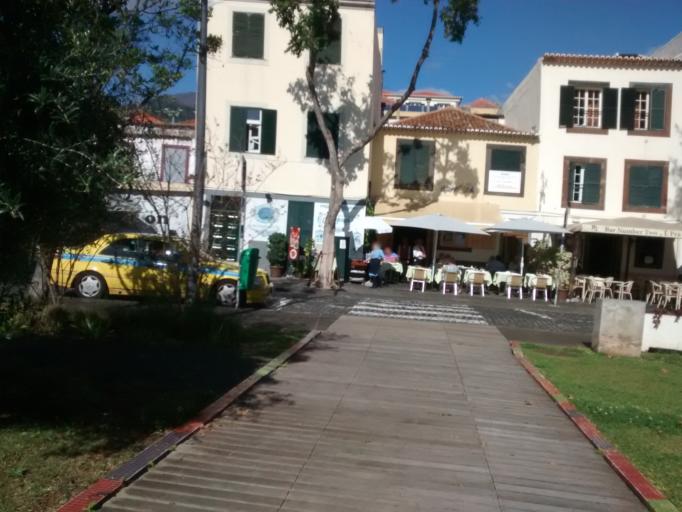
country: PT
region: Madeira
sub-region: Funchal
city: Funchal
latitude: 32.6475
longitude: -16.9013
